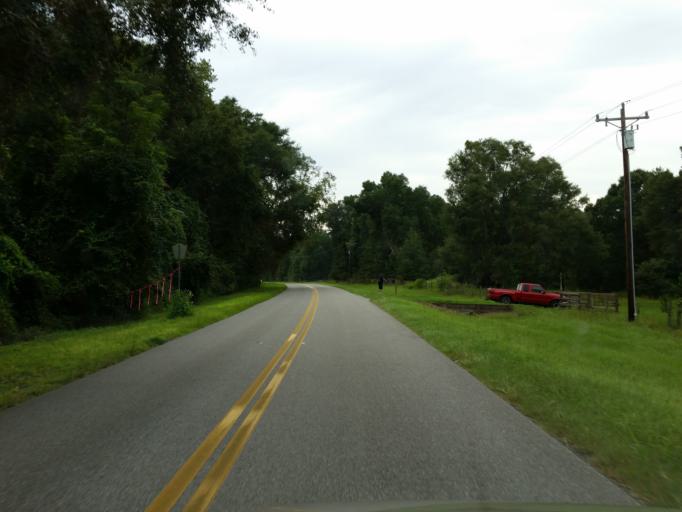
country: US
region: Florida
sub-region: Alachua County
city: High Springs
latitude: 29.9522
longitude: -82.5169
